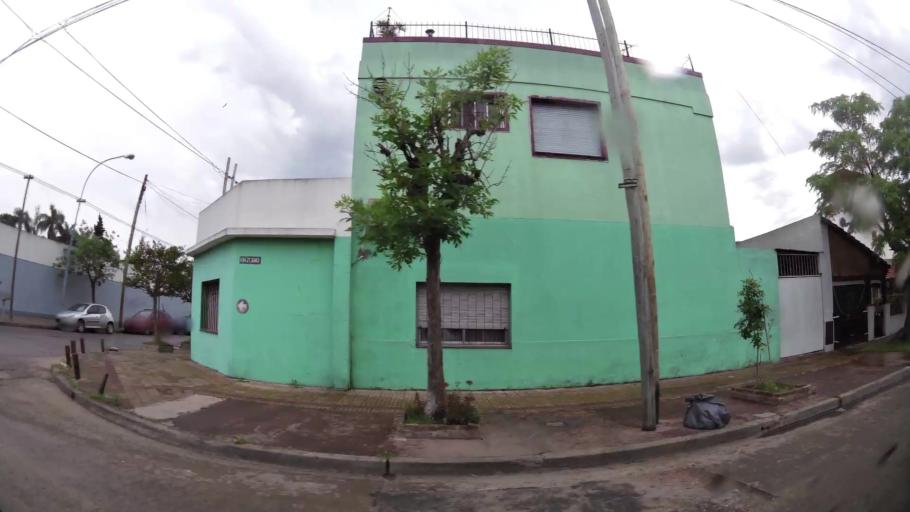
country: AR
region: Buenos Aires
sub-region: Partido de Lanus
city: Lanus
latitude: -34.6784
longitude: -58.4077
